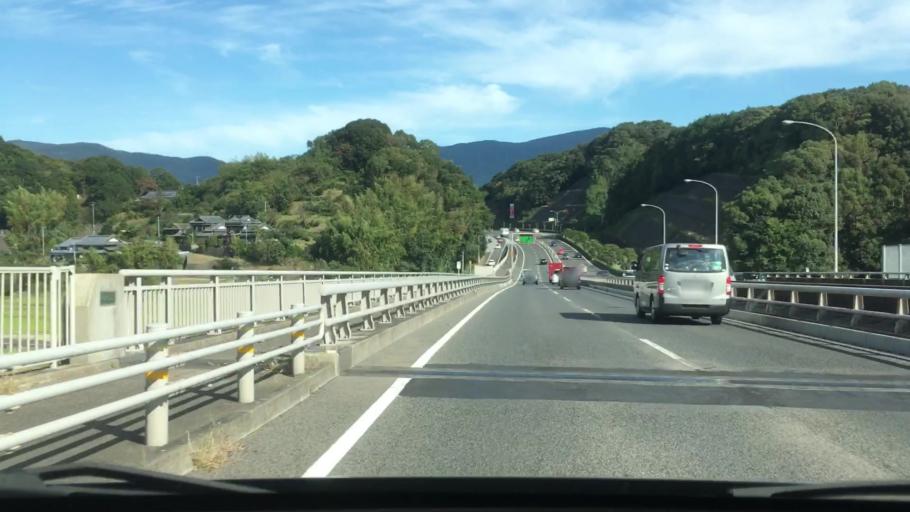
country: JP
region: Nagasaki
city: Sasebo
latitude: 33.1324
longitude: 129.7866
